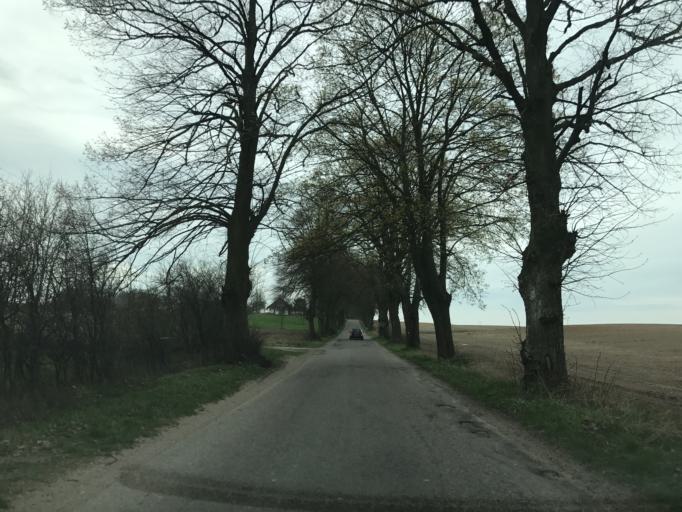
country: PL
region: Warmian-Masurian Voivodeship
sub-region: Powiat olsztynski
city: Olsztynek
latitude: 53.5978
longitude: 20.2740
